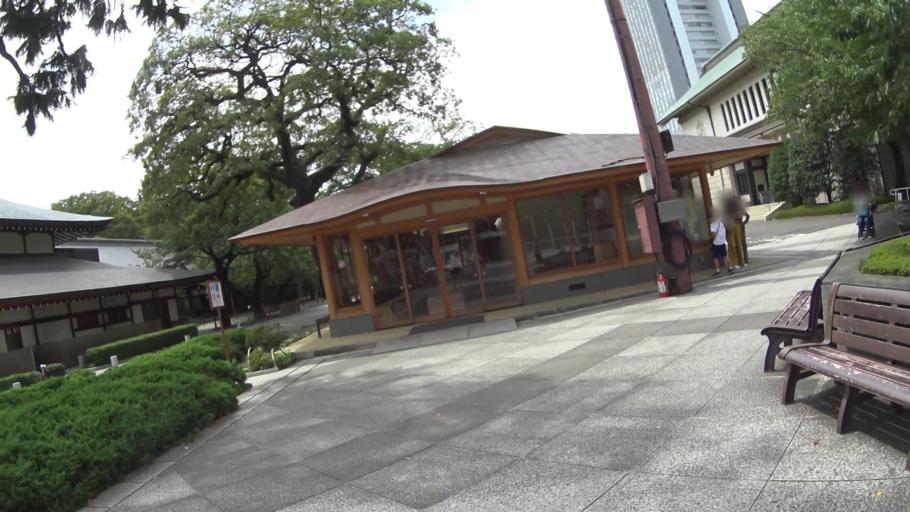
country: JP
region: Tokyo
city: Tokyo
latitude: 35.6949
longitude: 139.7431
